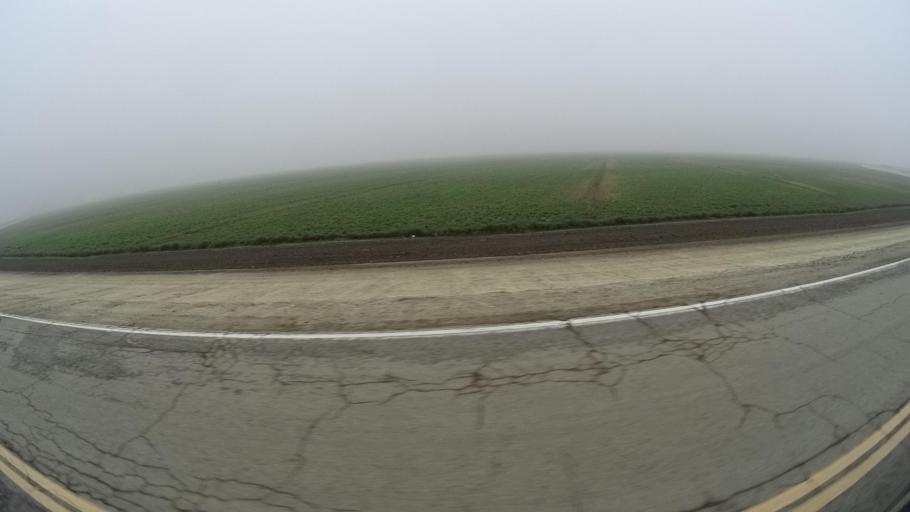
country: US
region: California
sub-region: Kern County
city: Buttonwillow
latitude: 35.4340
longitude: -119.5426
